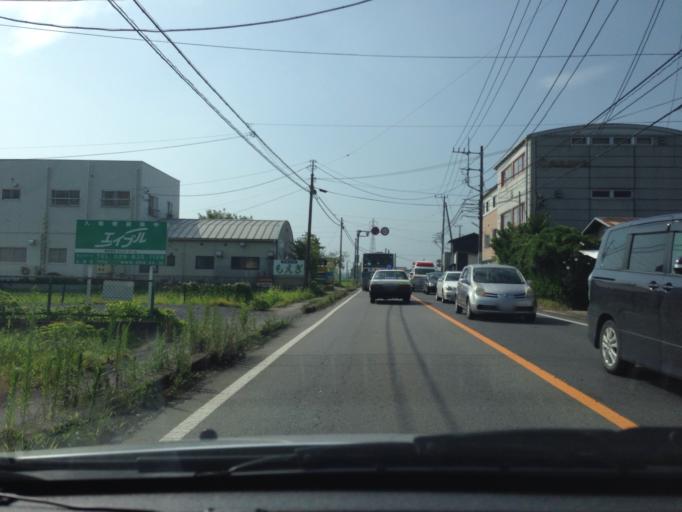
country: JP
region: Ibaraki
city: Ami
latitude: 36.0639
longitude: 140.2129
